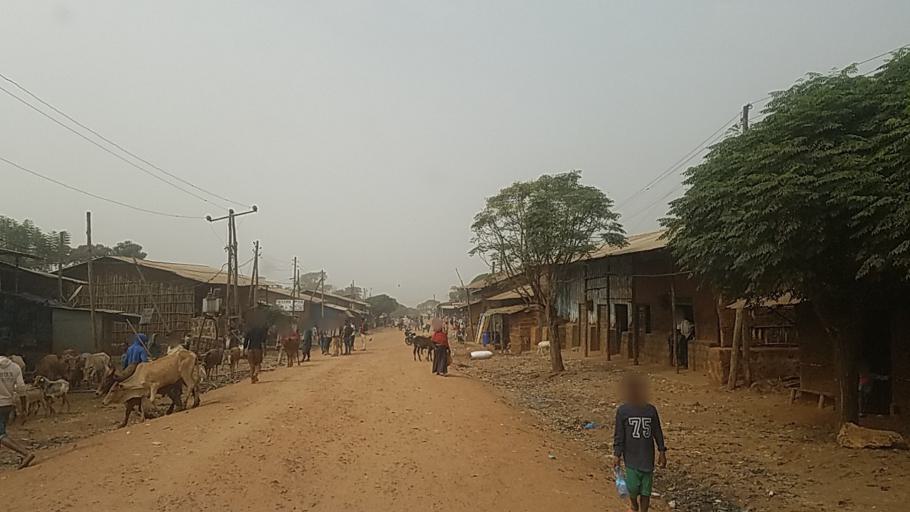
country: ET
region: Amhara
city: Bure
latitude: 10.8479
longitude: 36.3461
